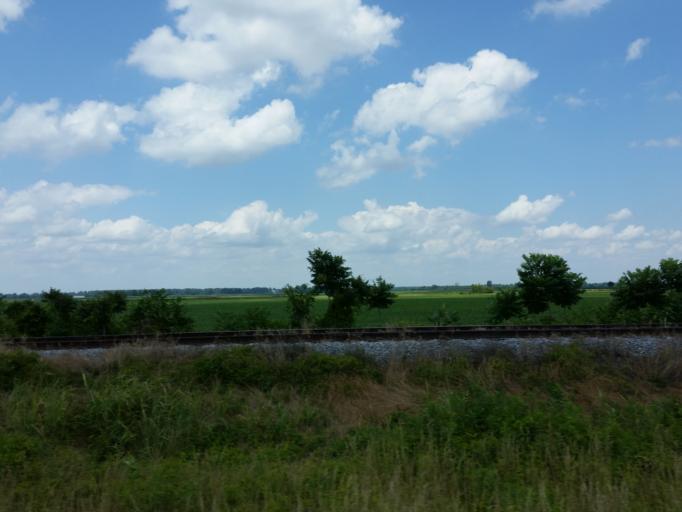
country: US
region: Tennessee
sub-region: Lake County
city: Tiptonville
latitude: 36.5035
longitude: -89.3557
